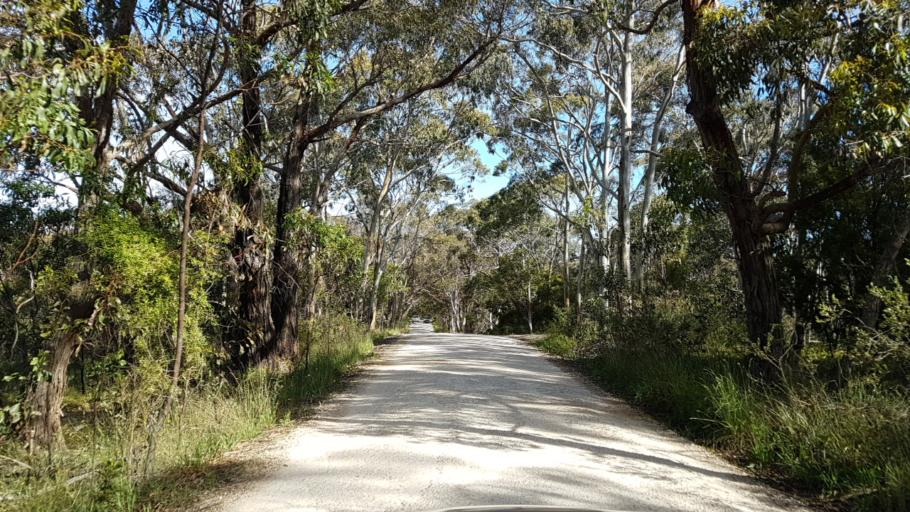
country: AU
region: South Australia
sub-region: Adelaide Hills
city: Adelaide Hills
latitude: -34.9080
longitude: 138.7486
